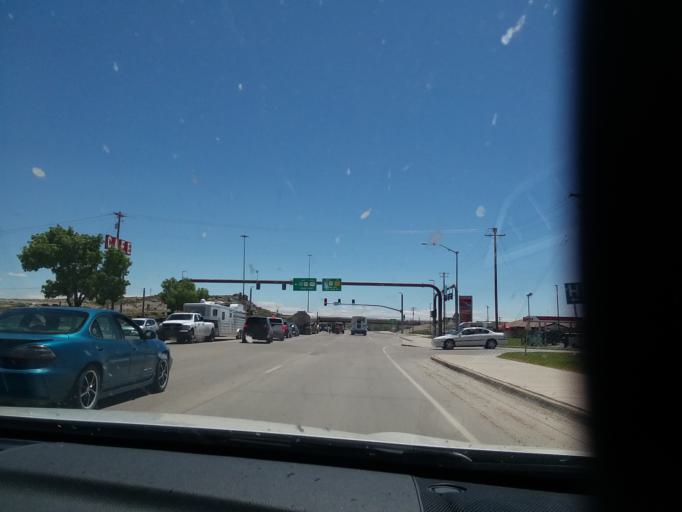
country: US
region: Wyoming
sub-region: Sweetwater County
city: Rock Springs
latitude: 41.6108
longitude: -109.2303
